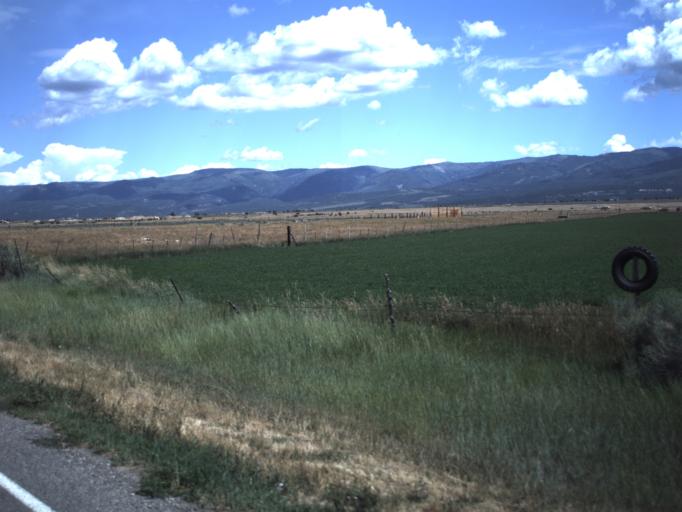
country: US
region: Utah
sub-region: Sanpete County
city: Mount Pleasant
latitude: 39.5010
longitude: -111.4884
